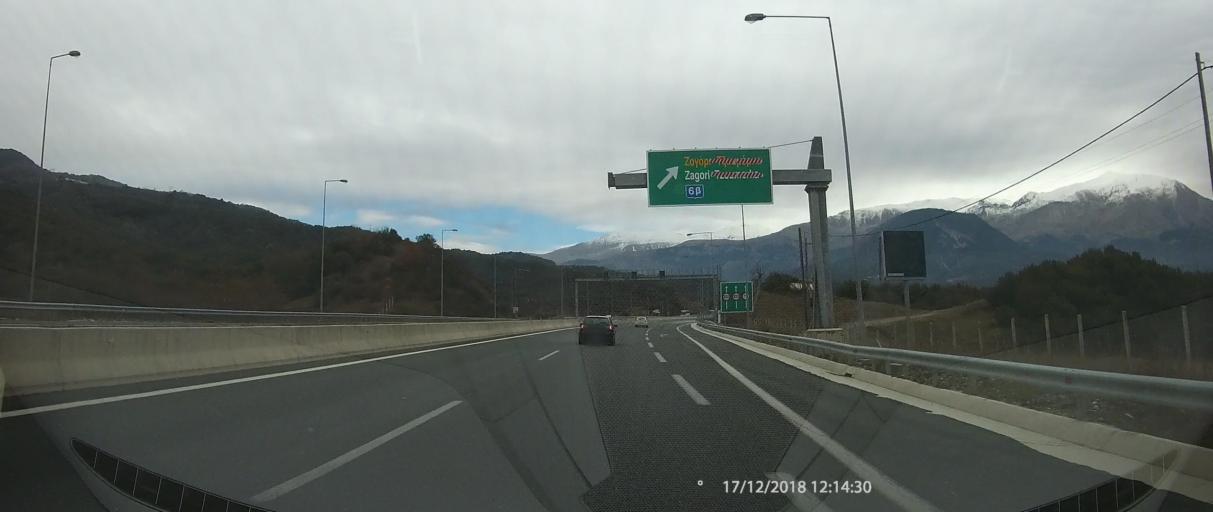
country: GR
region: Epirus
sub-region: Nomos Ioanninon
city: Katsikas
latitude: 39.7183
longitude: 20.9988
